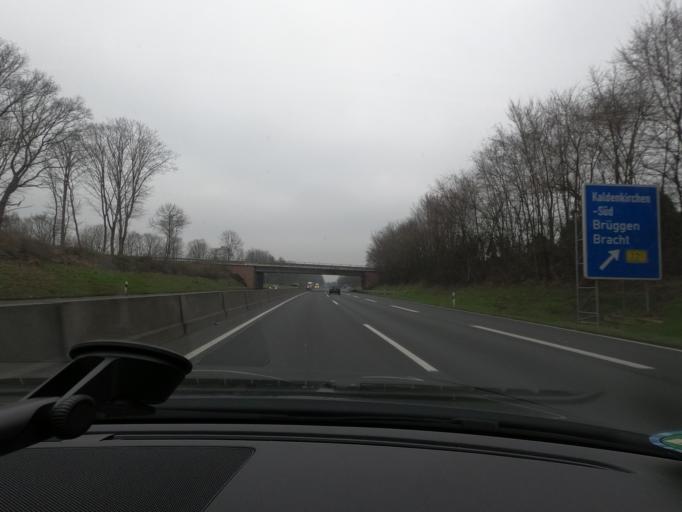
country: DE
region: North Rhine-Westphalia
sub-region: Regierungsbezirk Dusseldorf
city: Nettetal
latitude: 51.3118
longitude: 6.2258
